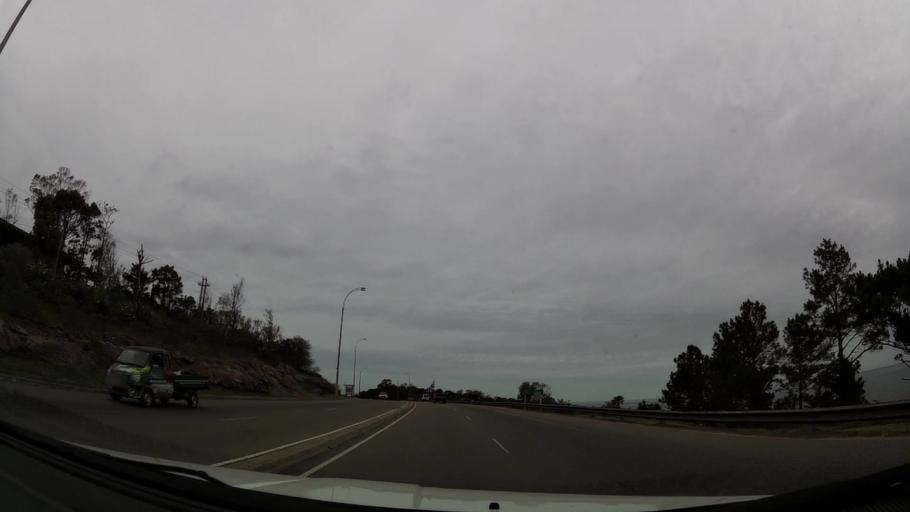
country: UY
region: Maldonado
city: Maldonado
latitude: -34.8941
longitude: -55.0384
